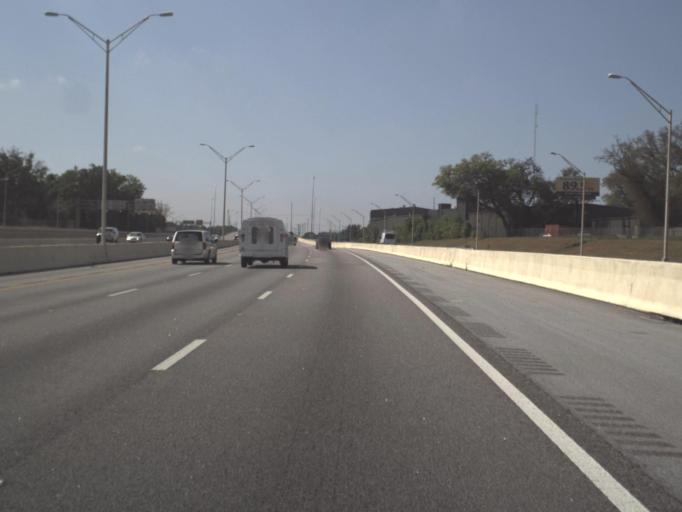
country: US
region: Florida
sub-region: Escambia County
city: Brent
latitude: 30.4795
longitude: -87.2304
